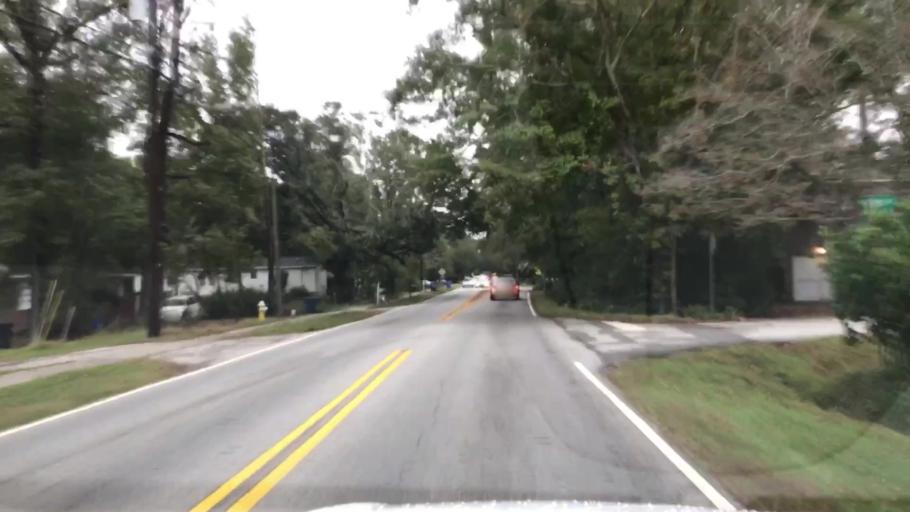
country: US
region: South Carolina
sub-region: Charleston County
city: North Charleston
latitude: 32.8146
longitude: -80.0033
